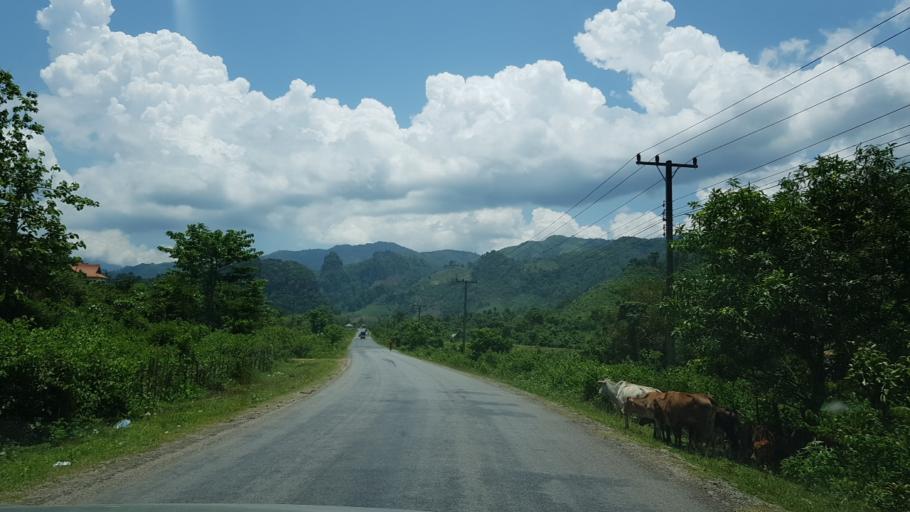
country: LA
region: Vientiane
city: Muang Kasi
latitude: 19.1275
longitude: 102.2406
